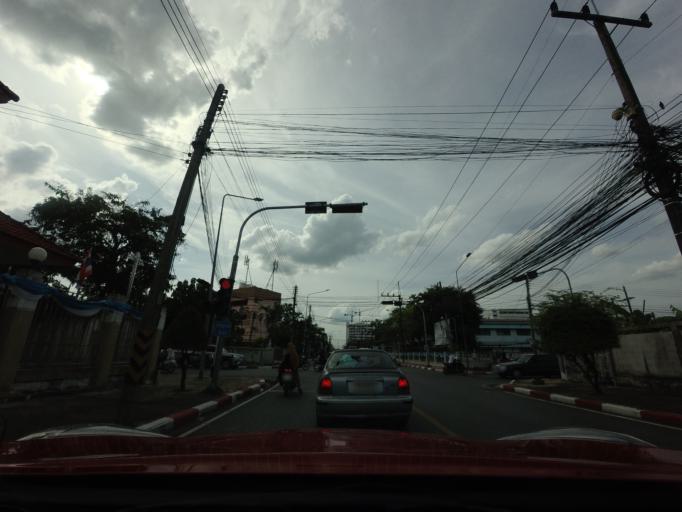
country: TH
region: Yala
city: Yala
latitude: 6.5439
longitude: 101.2784
